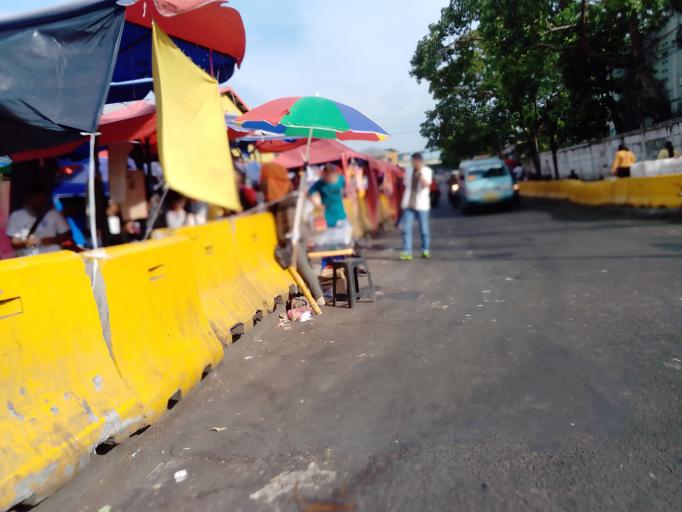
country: ID
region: Jakarta Raya
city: Jakarta
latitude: -6.1870
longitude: 106.8113
